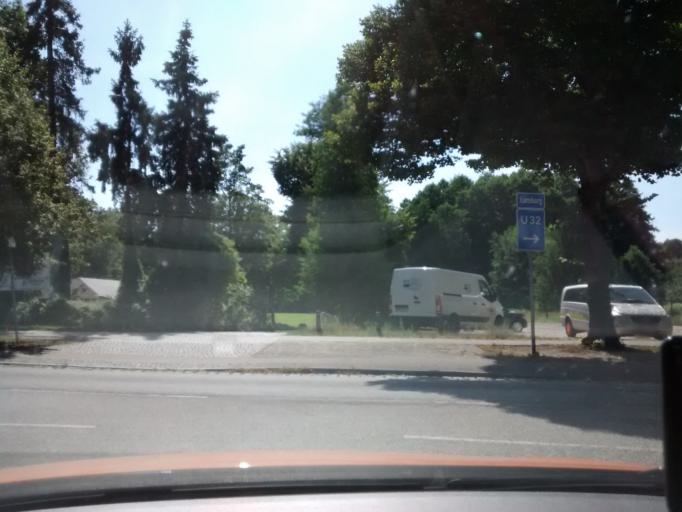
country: DE
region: Brandenburg
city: Birkenwerder
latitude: 52.6886
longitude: 13.2825
